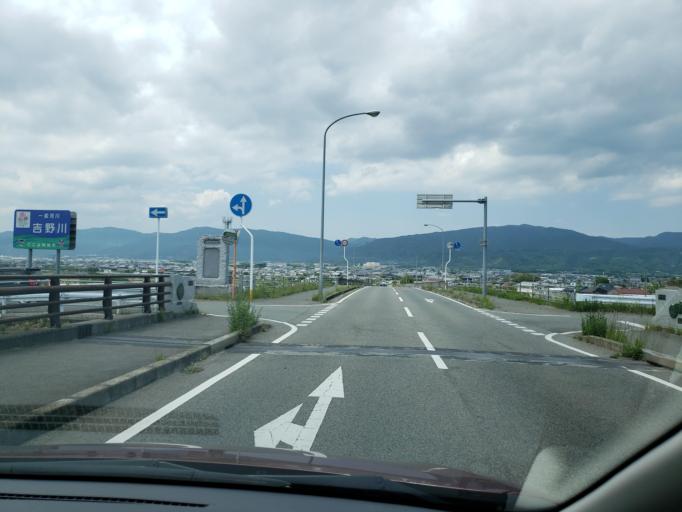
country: JP
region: Tokushima
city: Kamojimacho-jogejima
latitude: 34.0927
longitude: 134.3847
